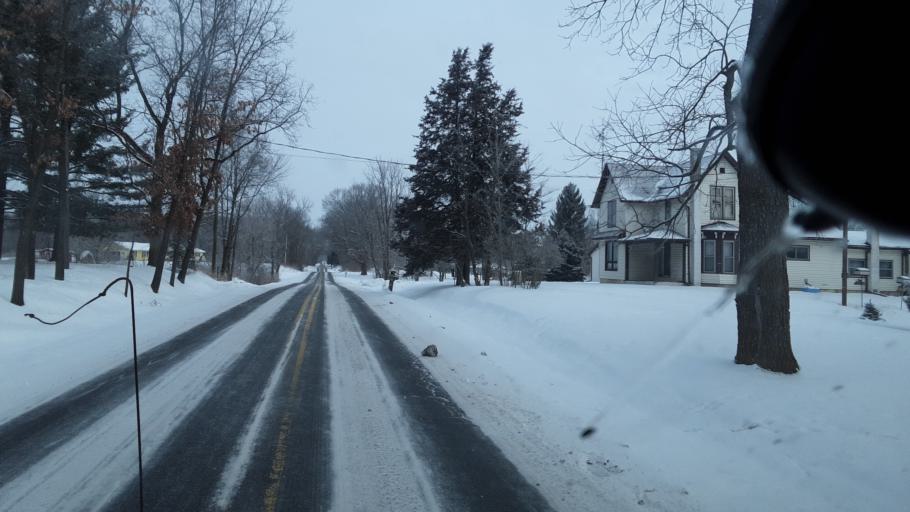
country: US
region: Michigan
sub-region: Jackson County
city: Jackson
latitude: 42.3071
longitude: -84.4829
